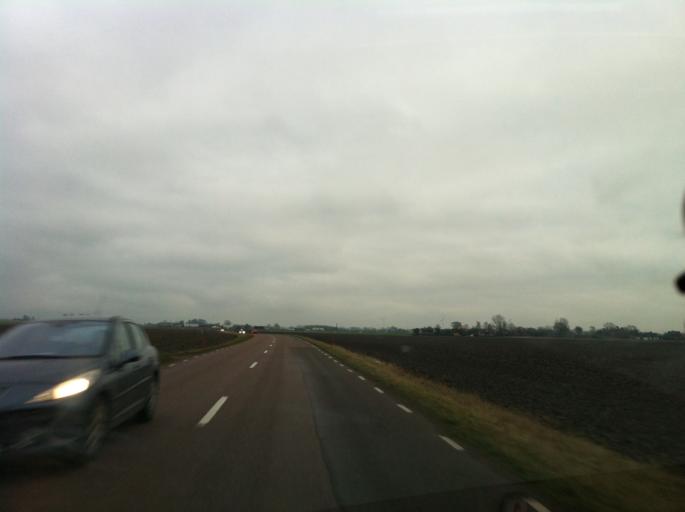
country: SE
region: Skane
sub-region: Landskrona
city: Landskrona
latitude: 55.9028
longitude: 12.8507
